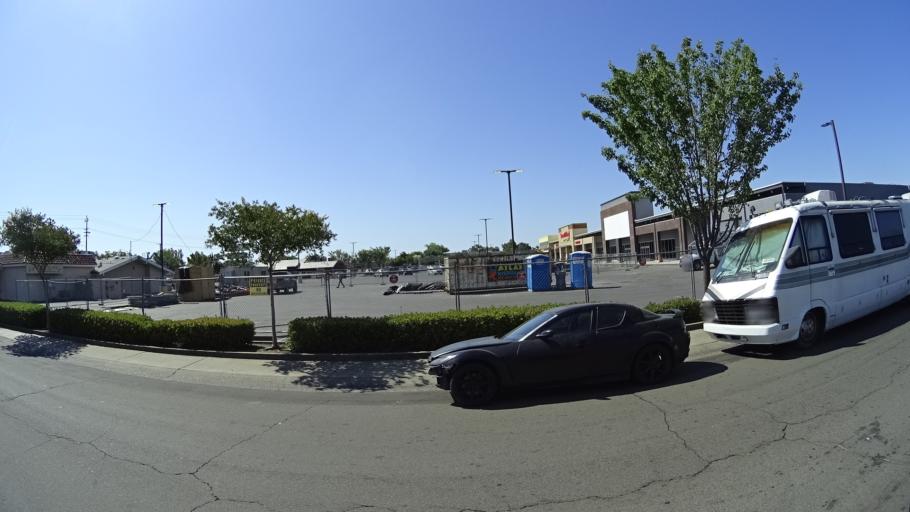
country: US
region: California
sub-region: Sacramento County
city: Parkway
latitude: 38.5296
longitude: -121.4459
